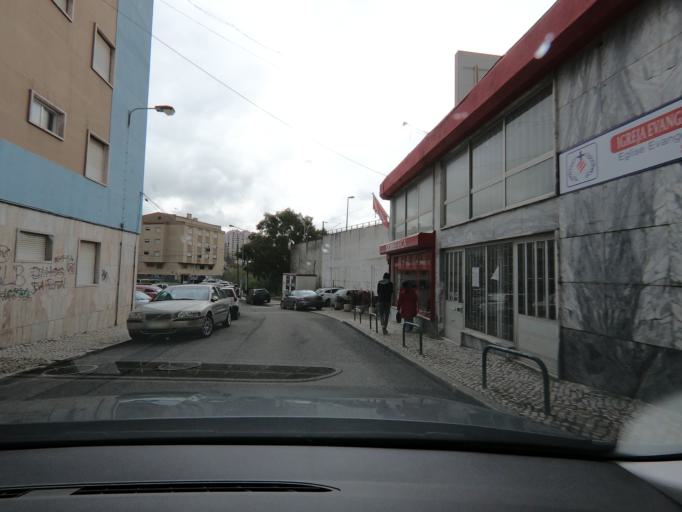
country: PT
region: Lisbon
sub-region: Sintra
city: Rio de Mouro
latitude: 38.7981
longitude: -9.3405
